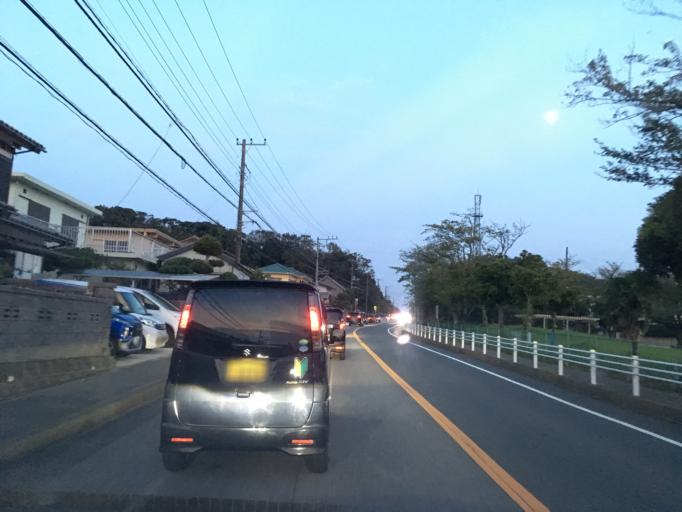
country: JP
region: Chiba
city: Kisarazu
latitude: 35.3465
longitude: 139.9152
